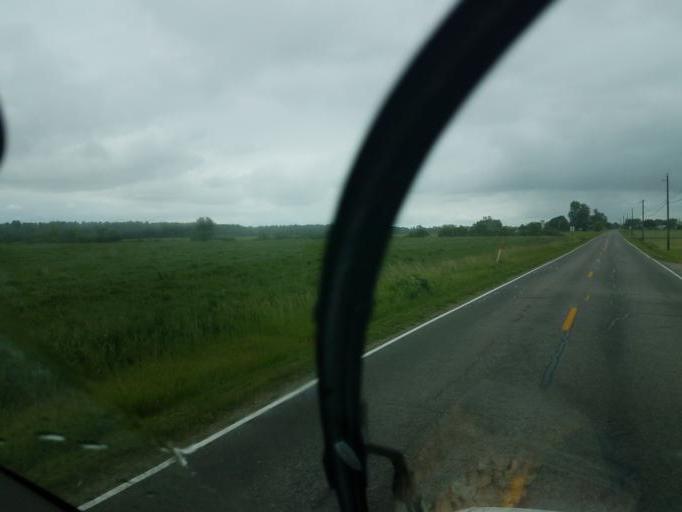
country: US
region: Ohio
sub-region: Marion County
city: Marion
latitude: 40.5644
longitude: -83.0177
